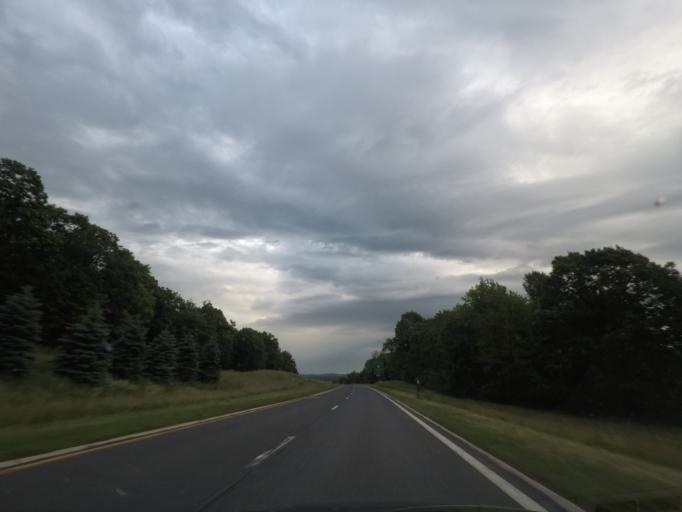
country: US
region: New York
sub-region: Columbia County
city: Philmont
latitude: 42.1909
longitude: -73.6405
